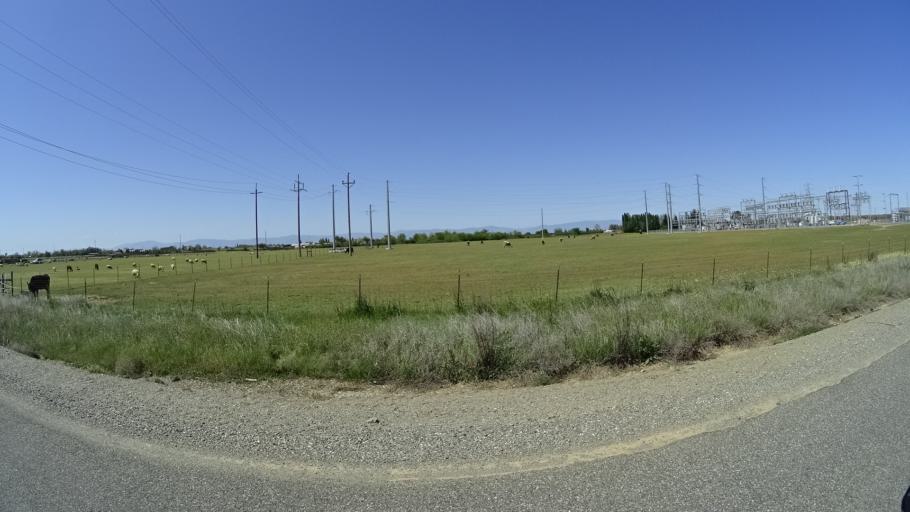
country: US
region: California
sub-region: Glenn County
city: Orland
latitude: 39.7760
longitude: -122.1408
